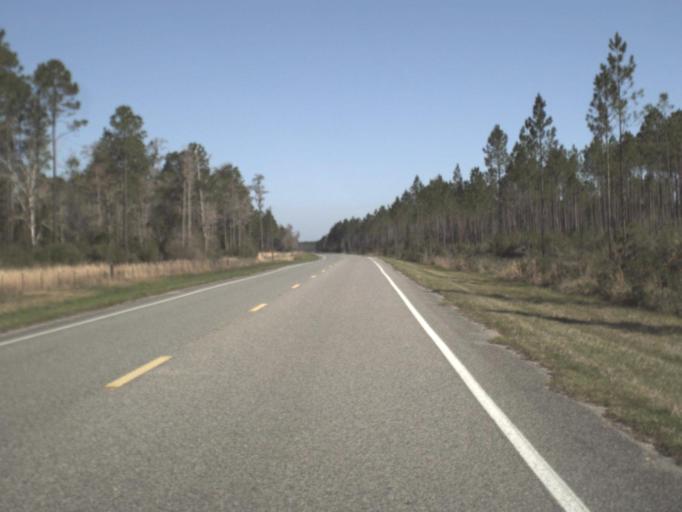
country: US
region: Florida
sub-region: Leon County
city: Woodville
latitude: 30.2672
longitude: -84.0421
